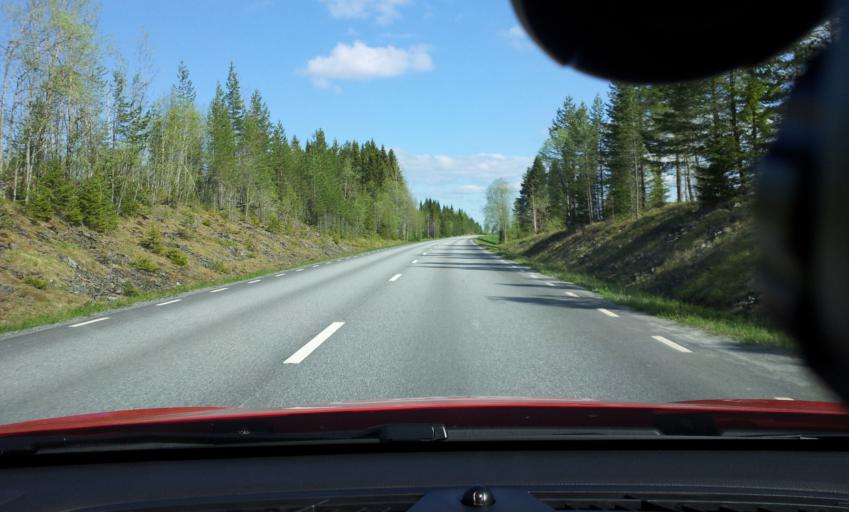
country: SE
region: Jaemtland
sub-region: Krokoms Kommun
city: Krokom
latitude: 63.1051
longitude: 14.2964
